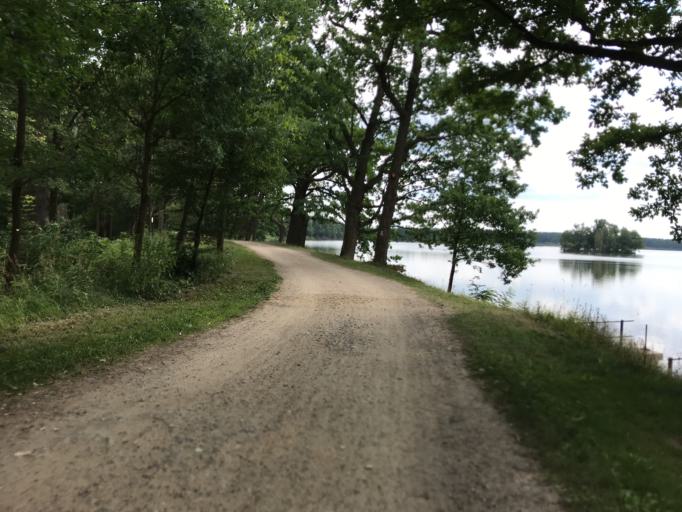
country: CZ
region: Jihocesky
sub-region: Okres Jindrichuv Hradec
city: Trebon
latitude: 48.9939
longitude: 14.7704
